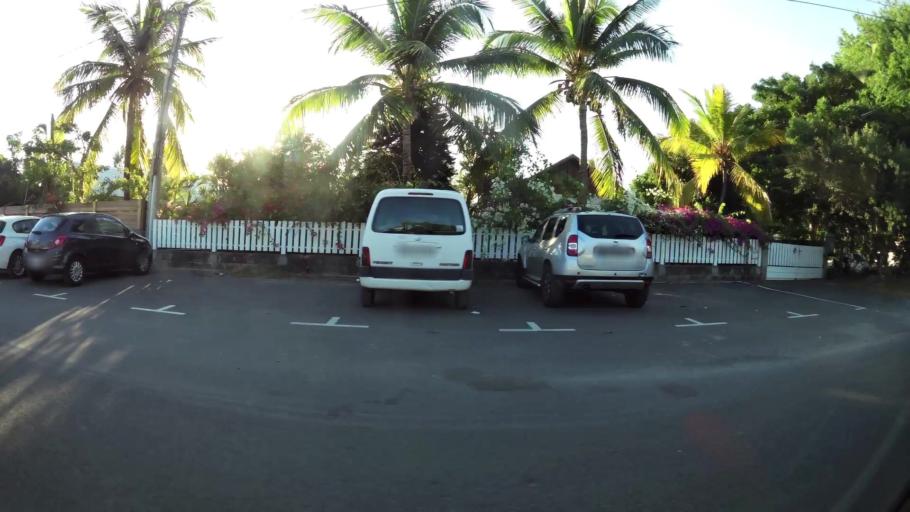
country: RE
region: Reunion
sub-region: Reunion
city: Trois-Bassins
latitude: -21.0943
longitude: 55.2390
